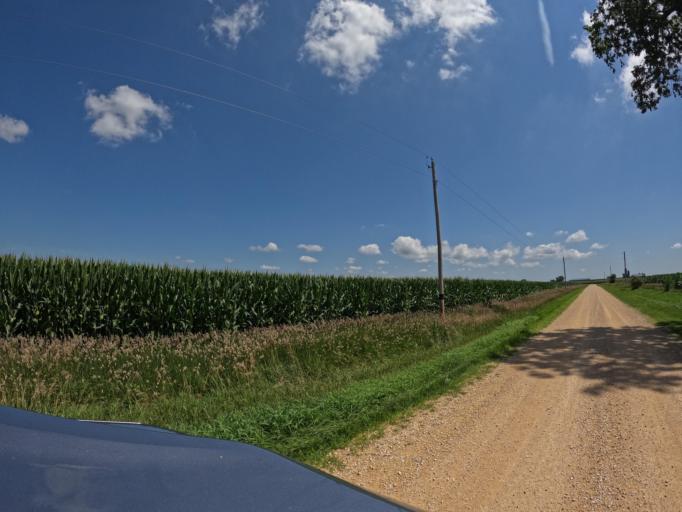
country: US
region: Iowa
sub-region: Clinton County
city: De Witt
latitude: 41.7784
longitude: -90.4169
